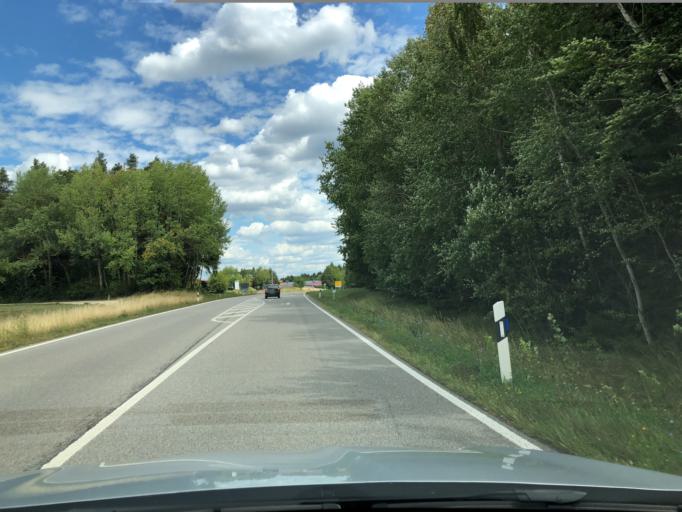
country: DE
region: Bavaria
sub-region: Upper Palatinate
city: Illschwang
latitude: 49.4555
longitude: 11.6723
